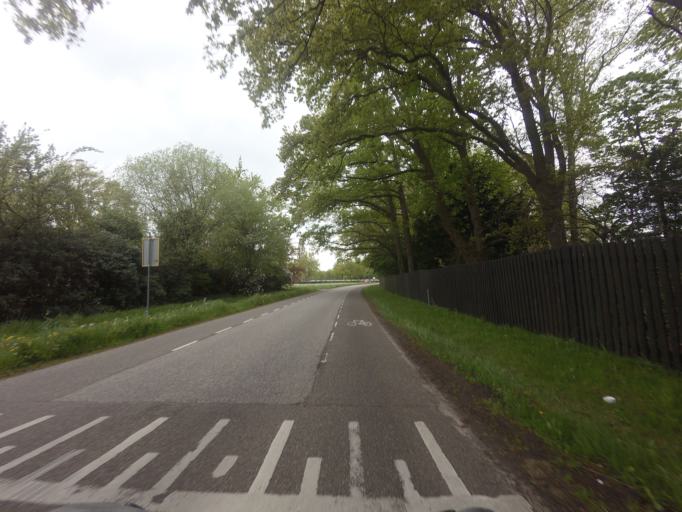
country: NL
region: Overijssel
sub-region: Gemeente Hof van Twente
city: Delden
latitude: 52.2673
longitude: 6.7096
